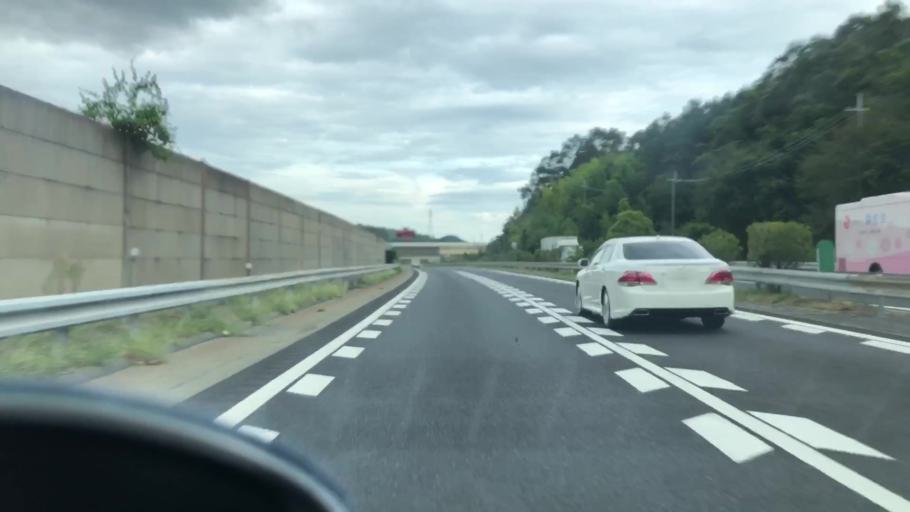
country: JP
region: Hyogo
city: Yashiro
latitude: 34.8984
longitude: 135.0732
